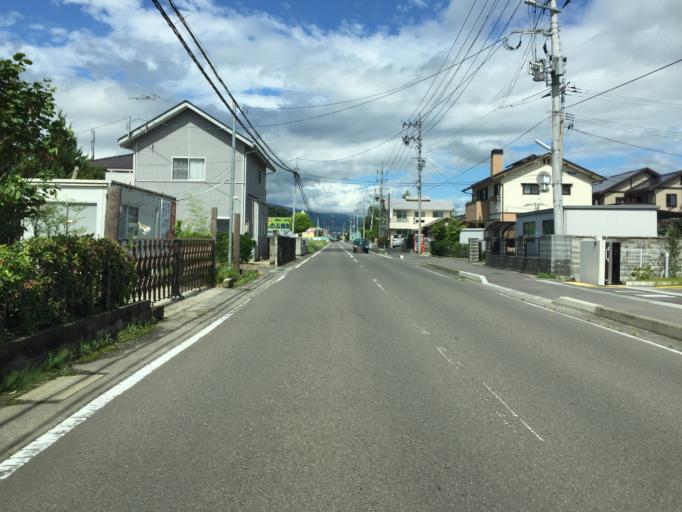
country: JP
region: Fukushima
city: Fukushima-shi
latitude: 37.7252
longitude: 140.4446
